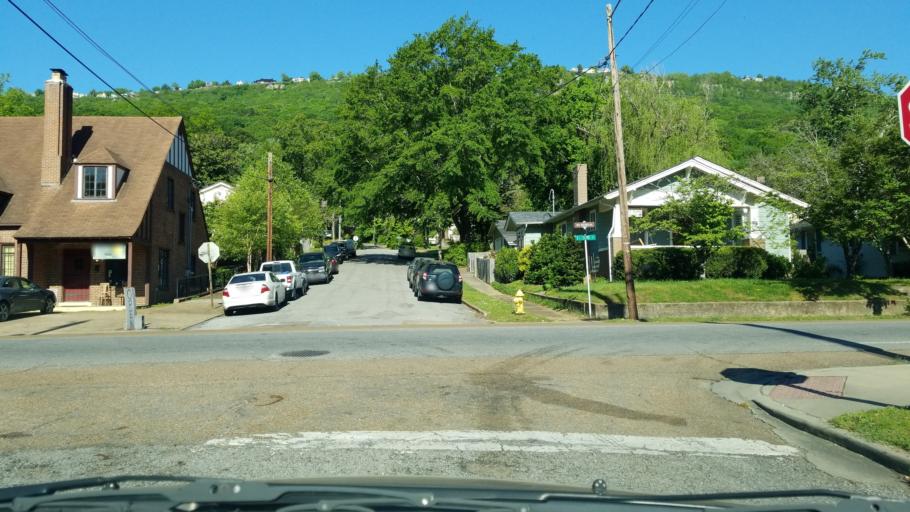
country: US
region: Tennessee
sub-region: Hamilton County
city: Lookout Mountain
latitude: 35.0004
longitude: -85.3292
